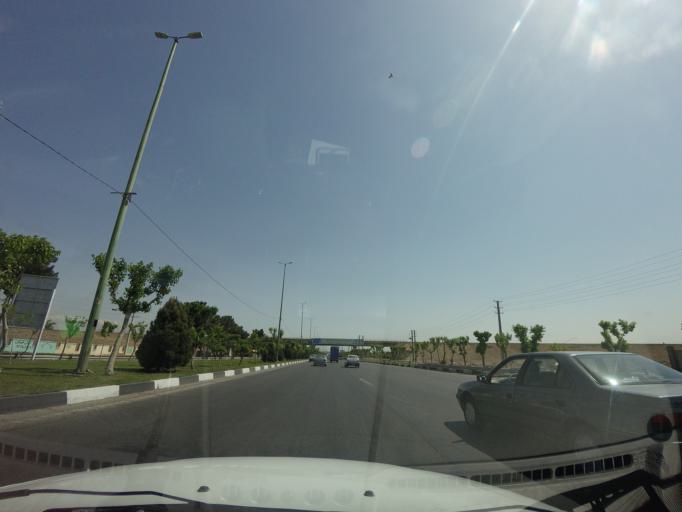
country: IR
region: Tehran
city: Eslamshahr
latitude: 35.5816
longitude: 51.2727
